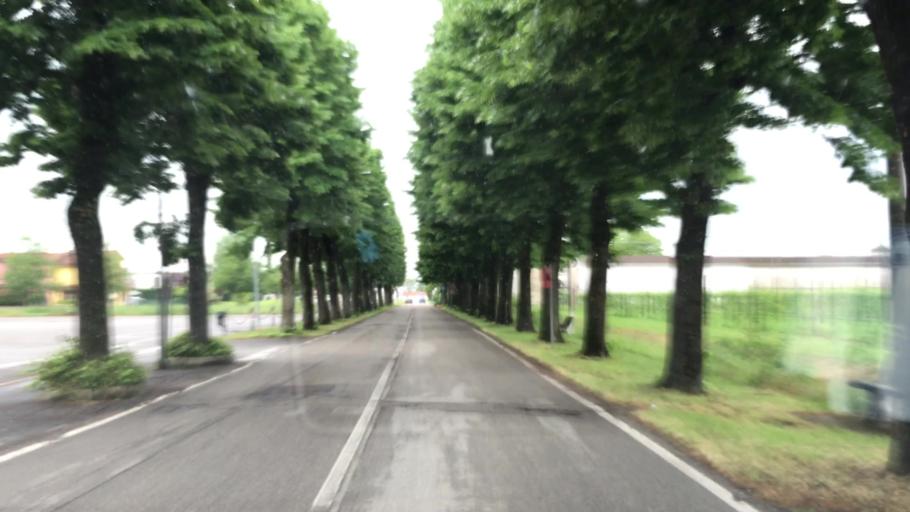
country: IT
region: Lombardy
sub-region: Provincia di Mantova
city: San Giovanni del Dosso
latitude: 44.9646
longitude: 11.0788
